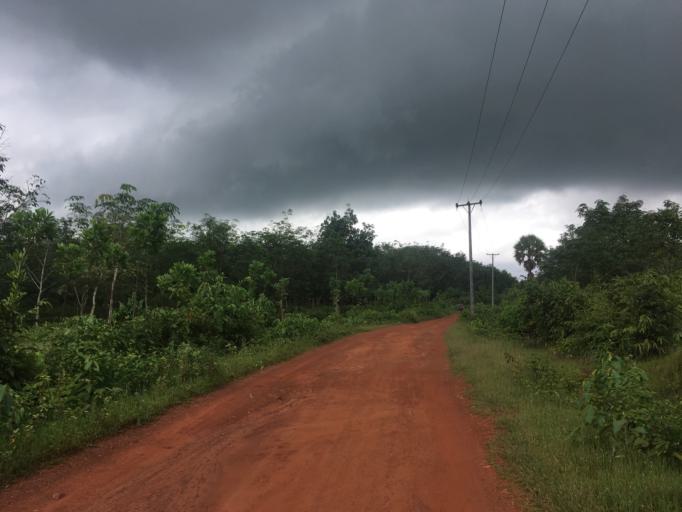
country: MM
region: Mon
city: Mawlamyine
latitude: 16.4573
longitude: 97.6840
